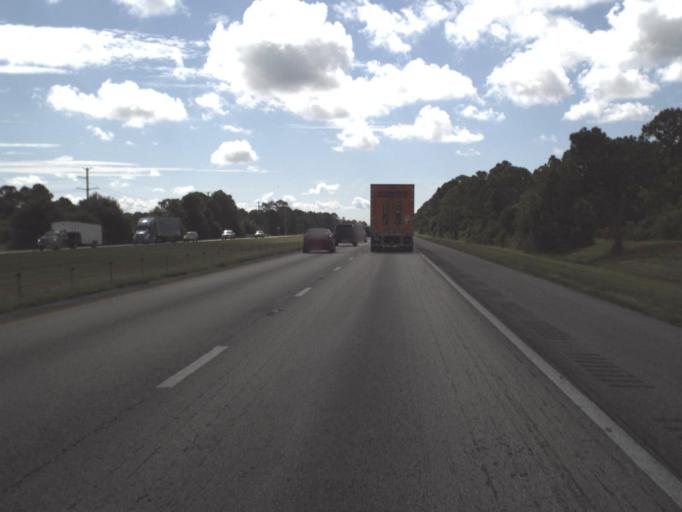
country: US
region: Florida
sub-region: Charlotte County
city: Port Charlotte
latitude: 27.0759
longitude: -82.1031
